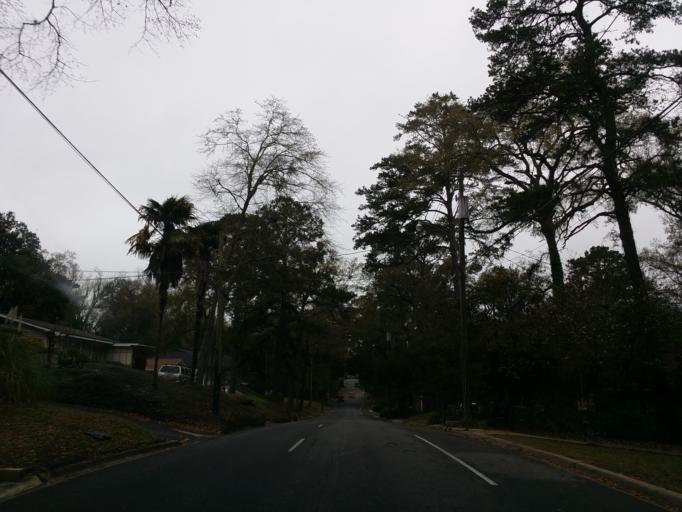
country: US
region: Florida
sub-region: Leon County
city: Tallahassee
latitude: 30.4574
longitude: -84.2730
